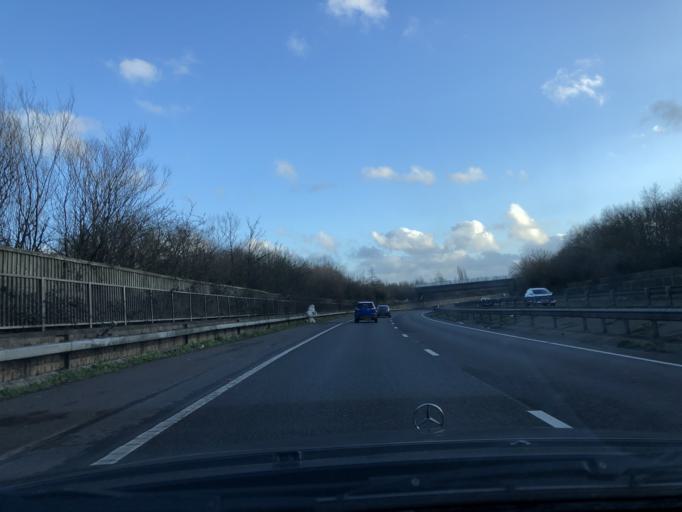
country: GB
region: England
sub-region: Hampshire
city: Aldershot
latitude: 51.2568
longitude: -0.7310
